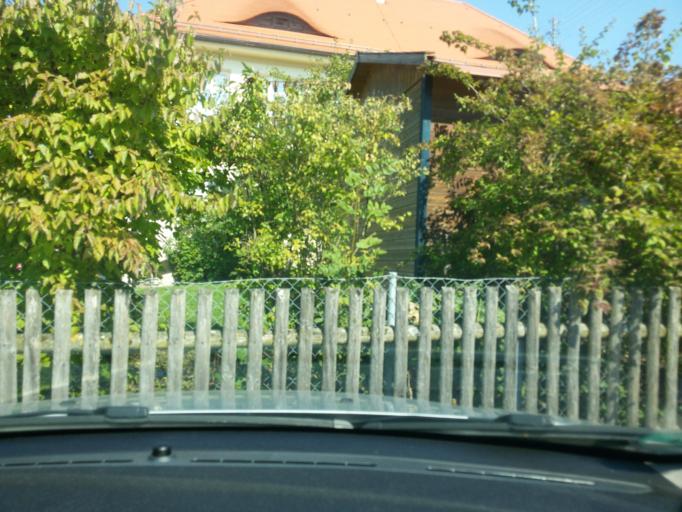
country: DE
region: Bavaria
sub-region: Swabia
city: Scherstetten
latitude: 48.1812
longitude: 10.6411
